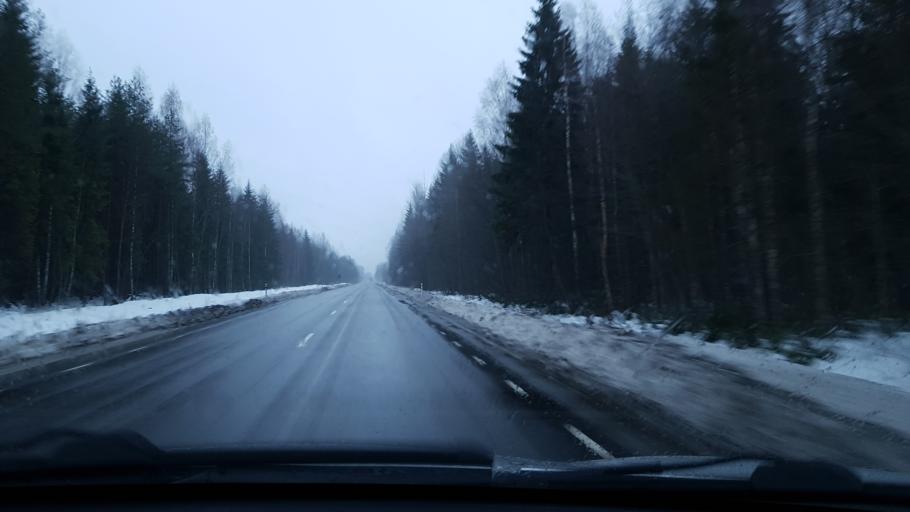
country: EE
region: Paernumaa
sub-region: Vaendra vald (alev)
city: Vandra
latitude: 58.8152
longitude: 25.1714
